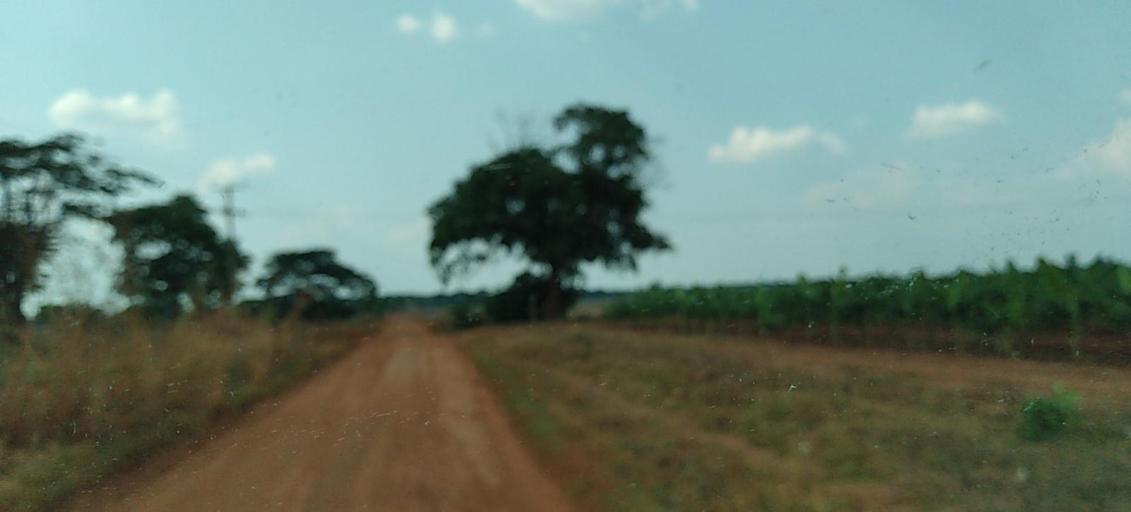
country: ZM
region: Copperbelt
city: Mpongwe
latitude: -13.5219
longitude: 28.0989
